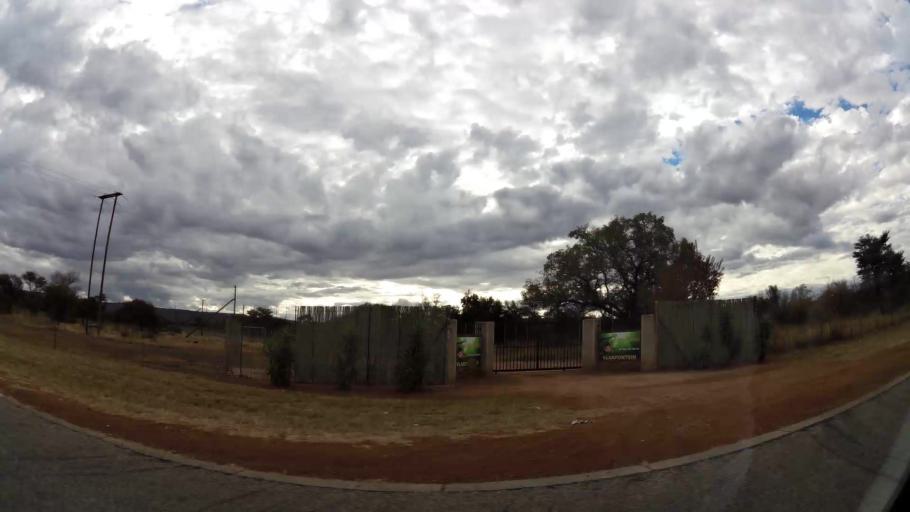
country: ZA
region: Limpopo
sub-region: Waterberg District Municipality
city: Modimolle
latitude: -24.5310
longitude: 28.7031
